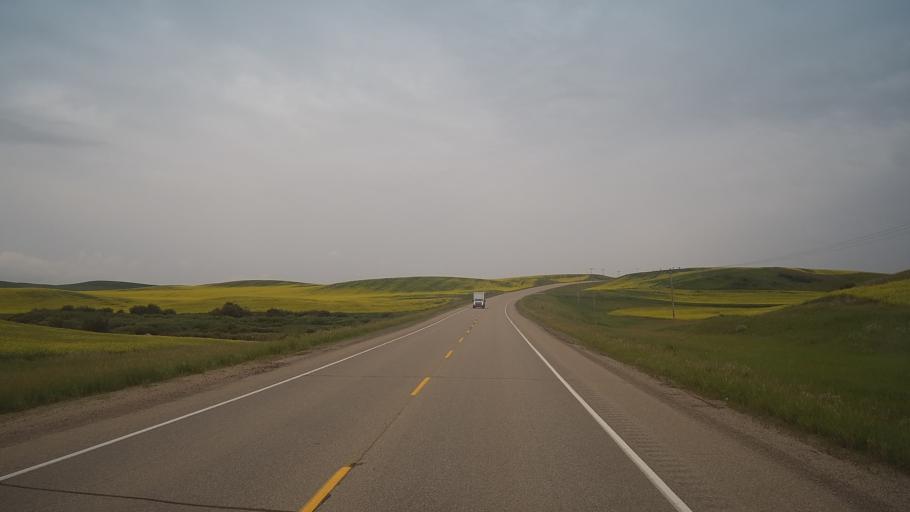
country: CA
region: Saskatchewan
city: Biggar
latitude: 52.0545
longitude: -107.7592
